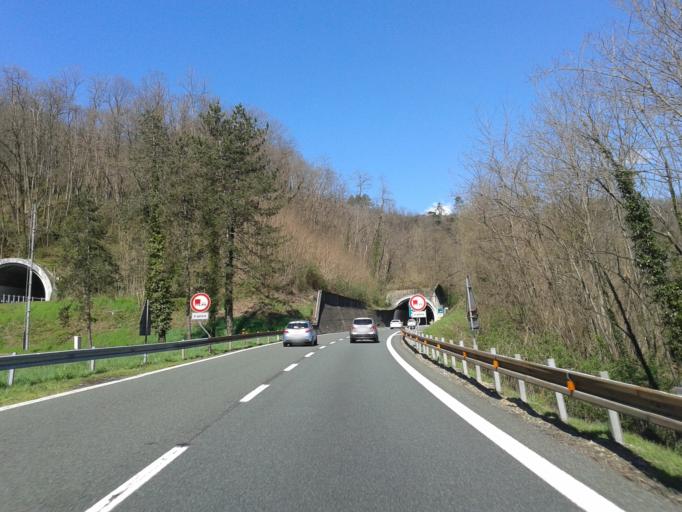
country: IT
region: Liguria
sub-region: Provincia di La Spezia
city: Borghetto di Vara
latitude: 44.2384
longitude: 9.6940
